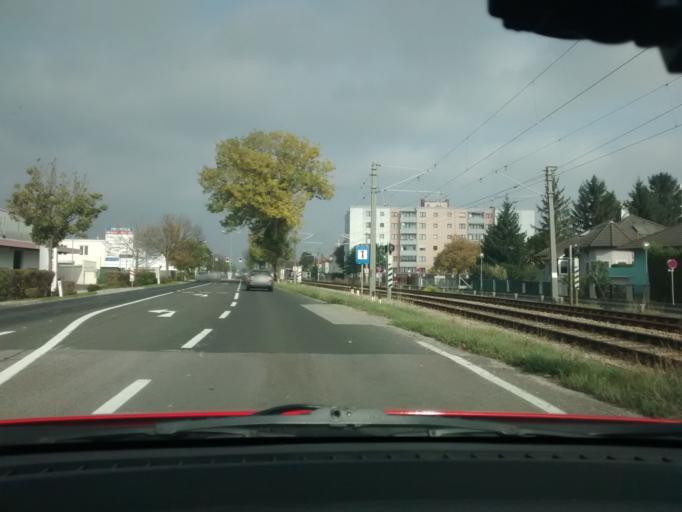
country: AT
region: Lower Austria
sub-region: Politischer Bezirk Baden
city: Traiskirchen
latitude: 48.0257
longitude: 16.2993
